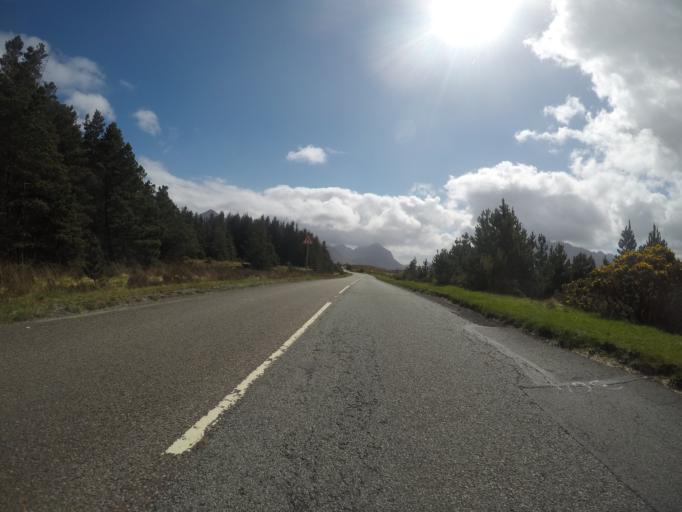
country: GB
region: Scotland
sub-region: Highland
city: Isle of Skye
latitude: 57.3143
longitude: -6.1991
